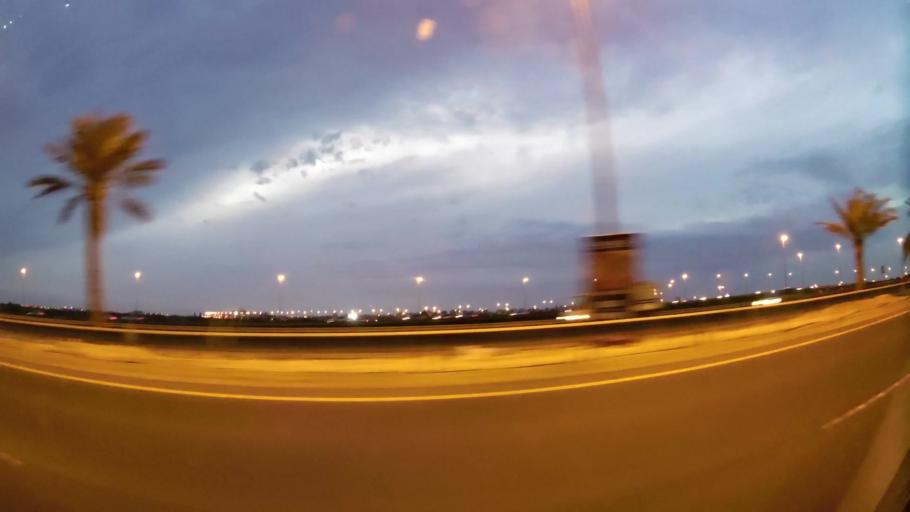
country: BH
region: Northern
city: Madinat `Isa
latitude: 26.1811
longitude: 50.5026
